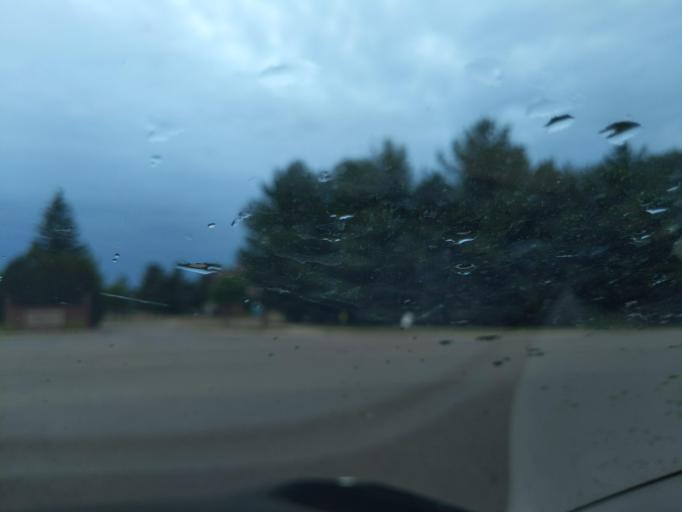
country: US
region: Michigan
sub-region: Clinton County
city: DeWitt
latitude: 42.8114
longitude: -84.6025
